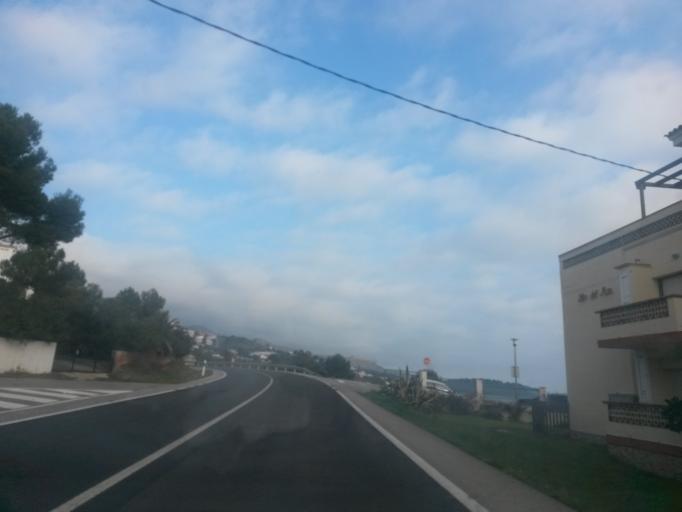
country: ES
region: Catalonia
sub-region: Provincia de Girona
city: Llanca
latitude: 42.3763
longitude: 3.1565
